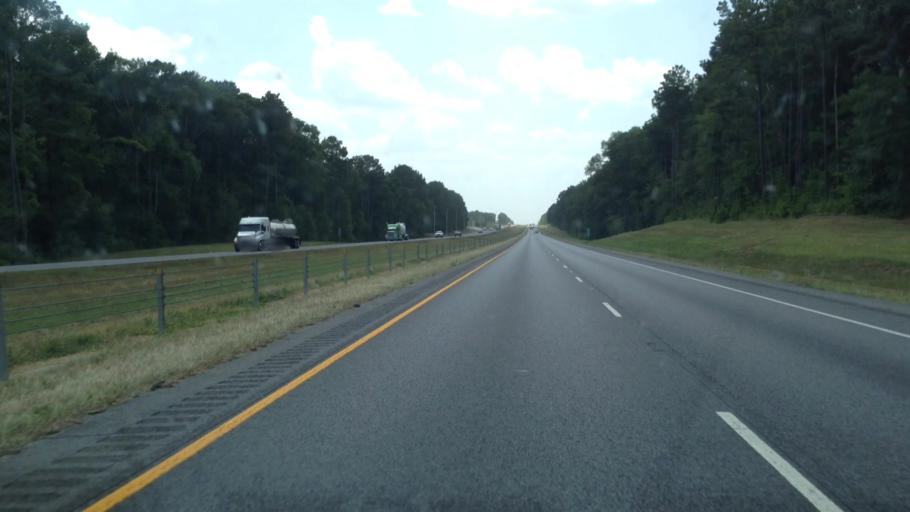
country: US
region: Louisiana
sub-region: Lincoln Parish
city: Ruston
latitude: 32.5306
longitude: -92.4612
